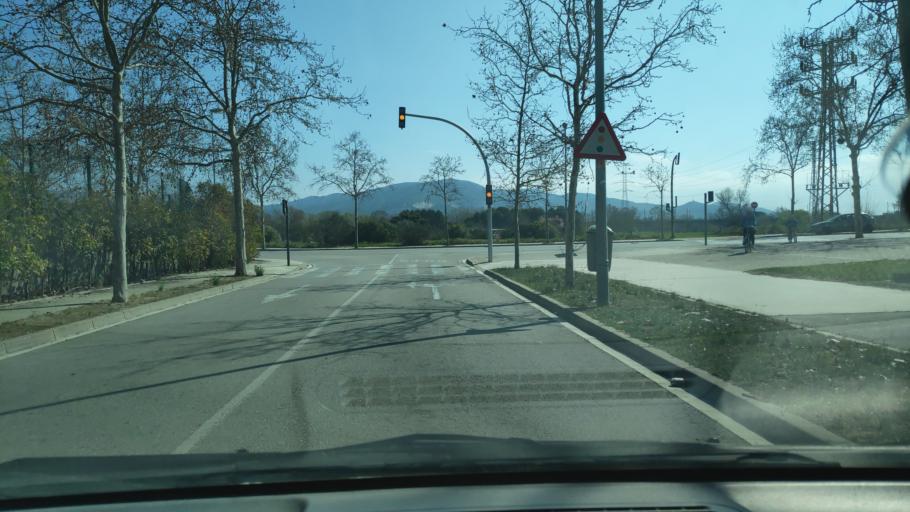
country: ES
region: Catalonia
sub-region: Provincia de Barcelona
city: Santa Perpetua de Mogoda
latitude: 41.5313
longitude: 2.1917
